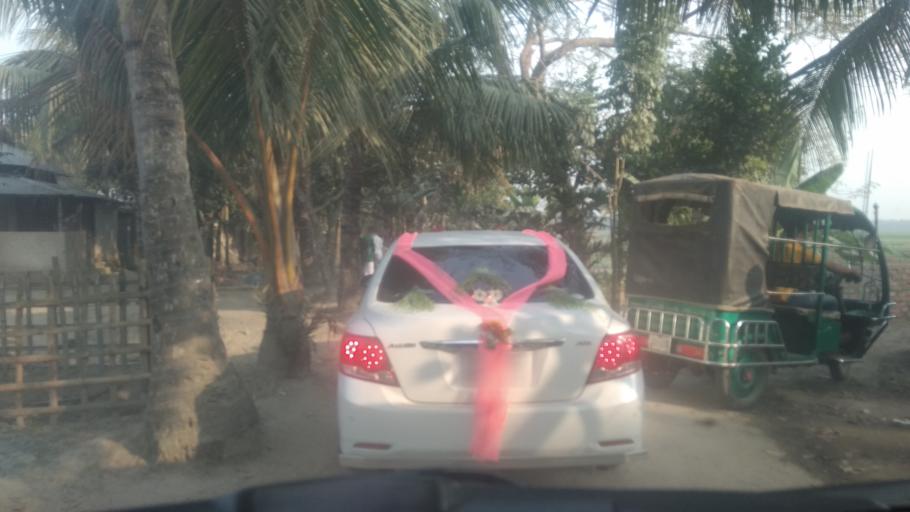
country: BD
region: Dhaka
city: Netrakona
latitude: 24.7748
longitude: 90.6082
